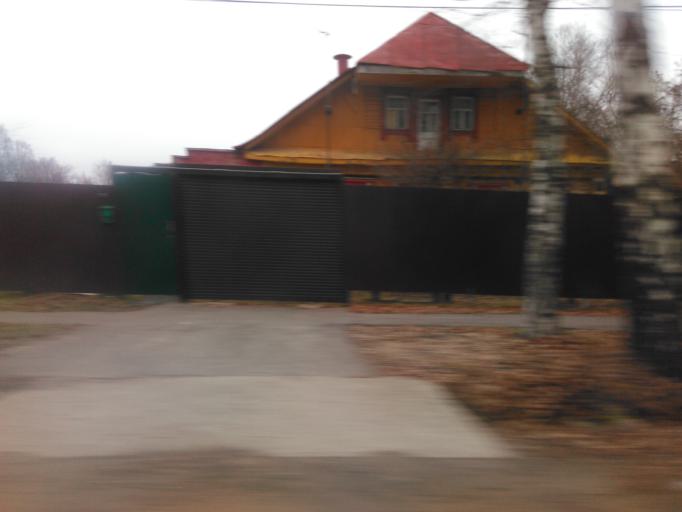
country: RU
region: Moskovskaya
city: Ashukino
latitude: 56.1660
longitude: 37.9443
